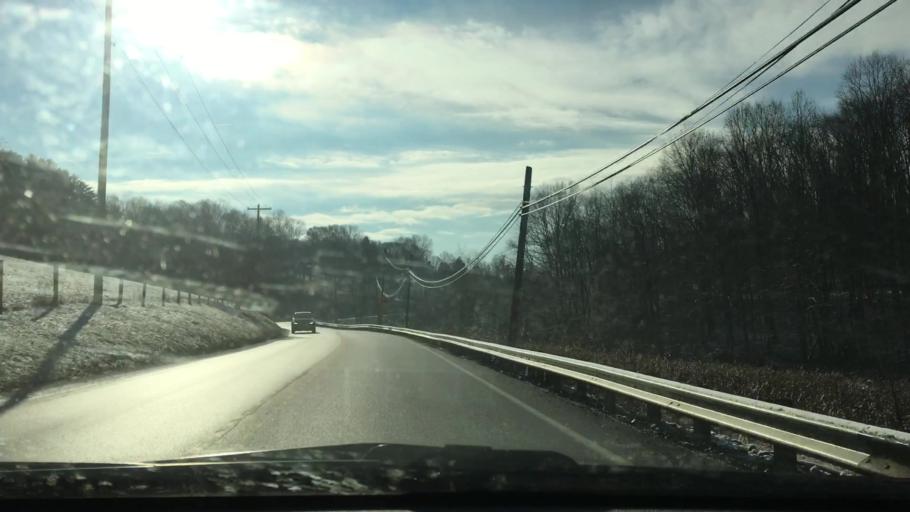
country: US
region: Pennsylvania
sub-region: Allegheny County
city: Oakdale
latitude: 40.4267
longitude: -80.2021
